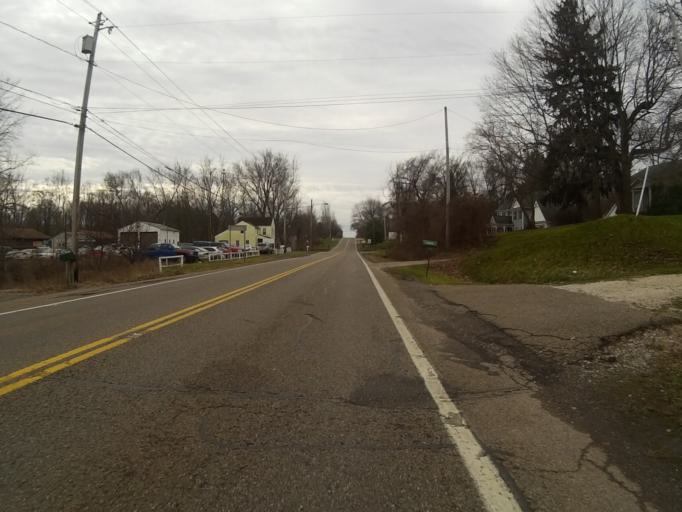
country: US
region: Ohio
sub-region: Summit County
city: Mogadore
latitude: 41.0222
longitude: -81.3474
